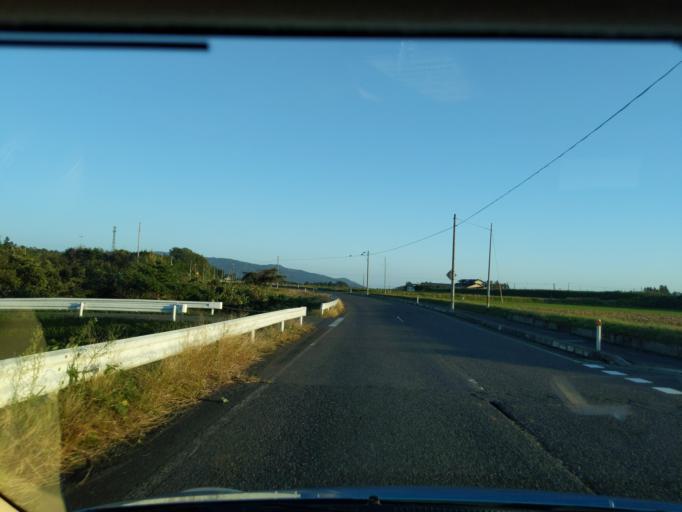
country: JP
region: Iwate
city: Mizusawa
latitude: 39.0693
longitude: 141.0958
